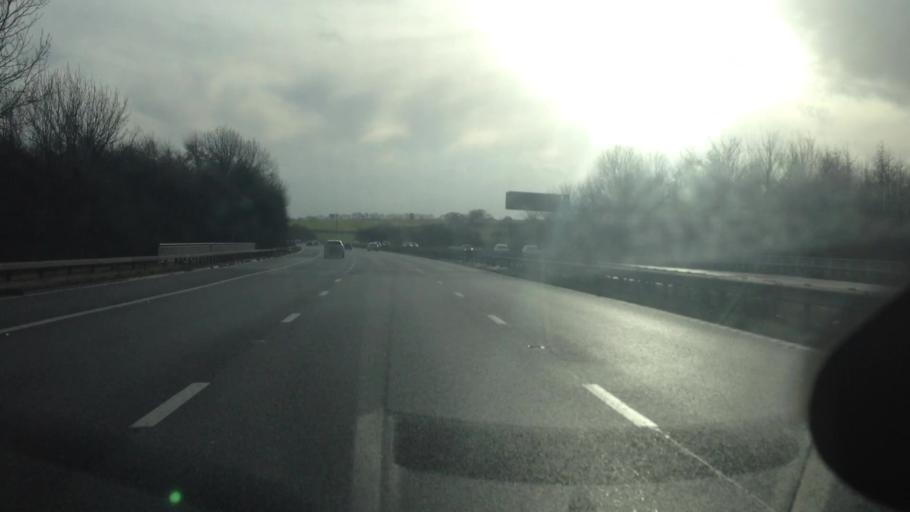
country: GB
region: England
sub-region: Barnsley
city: Darton
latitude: 53.6041
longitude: -1.5514
